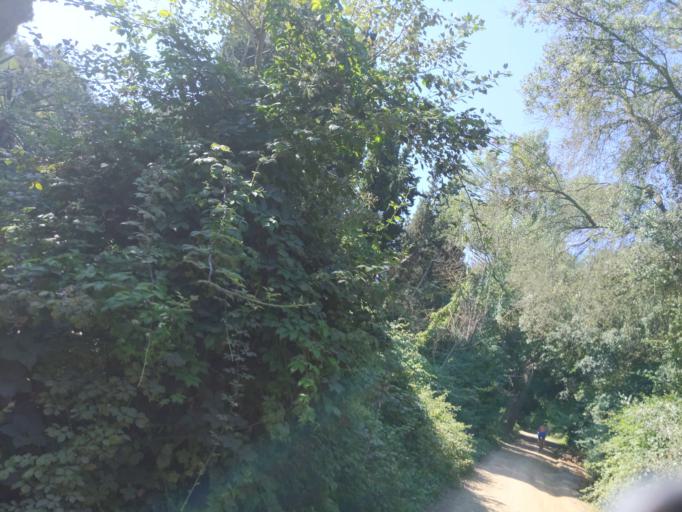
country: ES
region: Catalonia
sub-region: Provincia de Barcelona
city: Nou Barris
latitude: 41.4576
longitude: 2.1515
